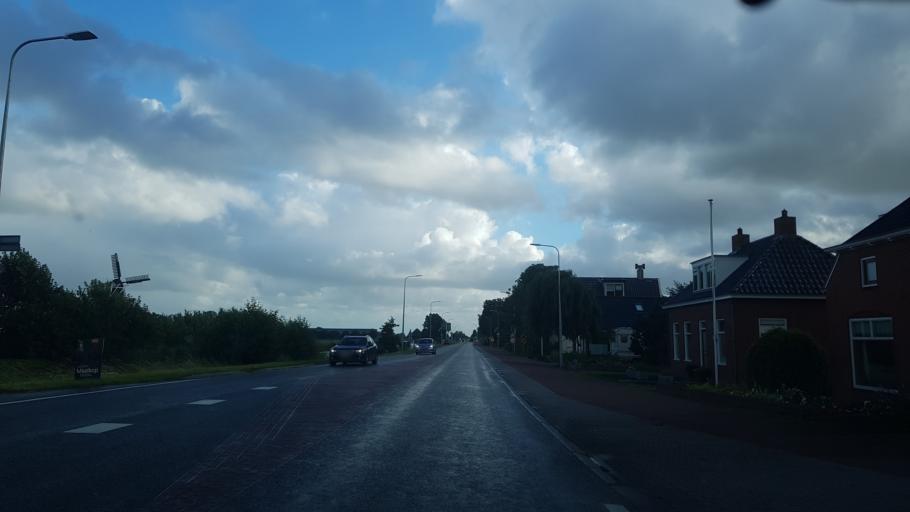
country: NL
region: Groningen
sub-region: Gemeente Bedum
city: Bedum
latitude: 53.2733
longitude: 6.6985
